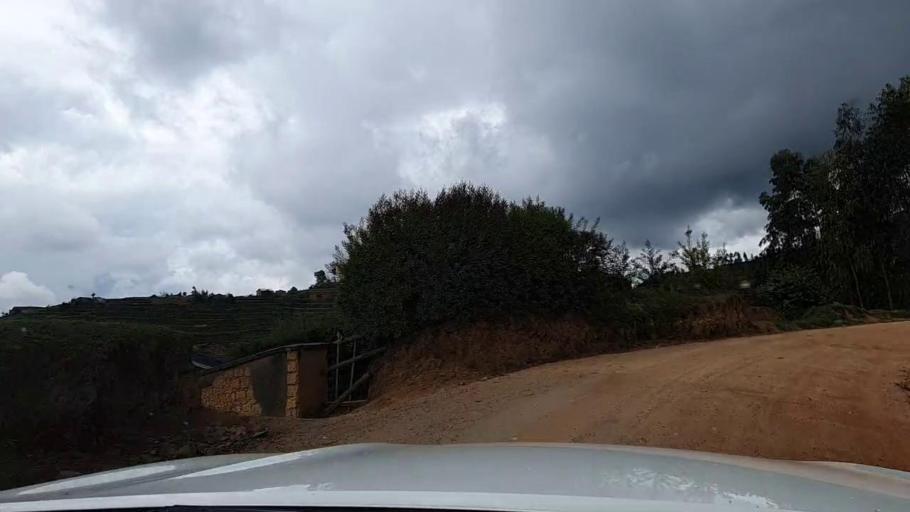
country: RW
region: Southern Province
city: Nzega
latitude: -2.4301
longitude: 29.4386
